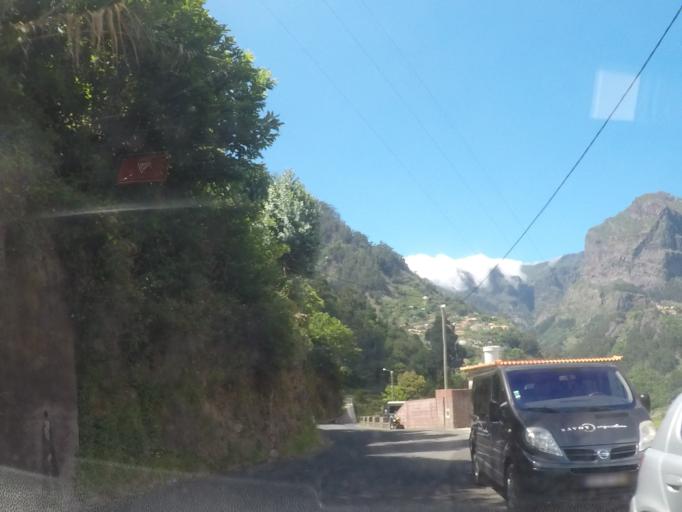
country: PT
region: Madeira
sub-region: Camara de Lobos
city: Curral das Freiras
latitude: 32.7095
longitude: -16.9731
